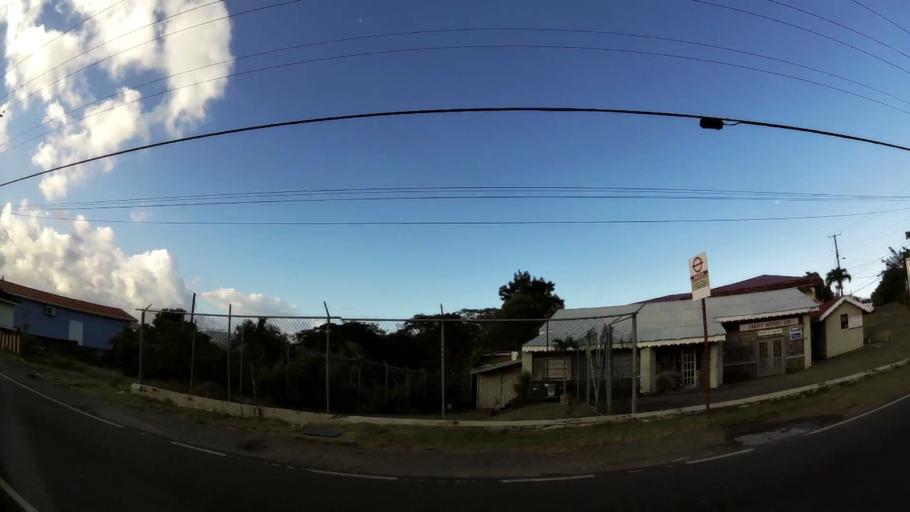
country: LC
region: Castries Quarter
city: Bisee
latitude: 14.0452
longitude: -60.9698
